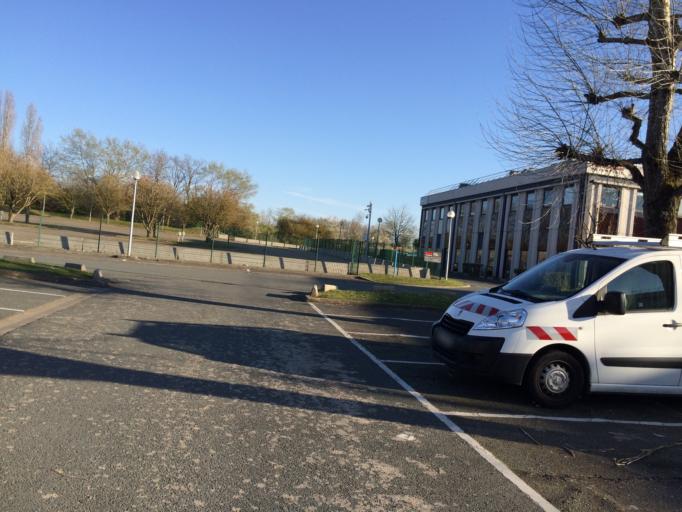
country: FR
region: Ile-de-France
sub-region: Departement de l'Essonne
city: Villejust
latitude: 48.6892
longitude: 2.2164
